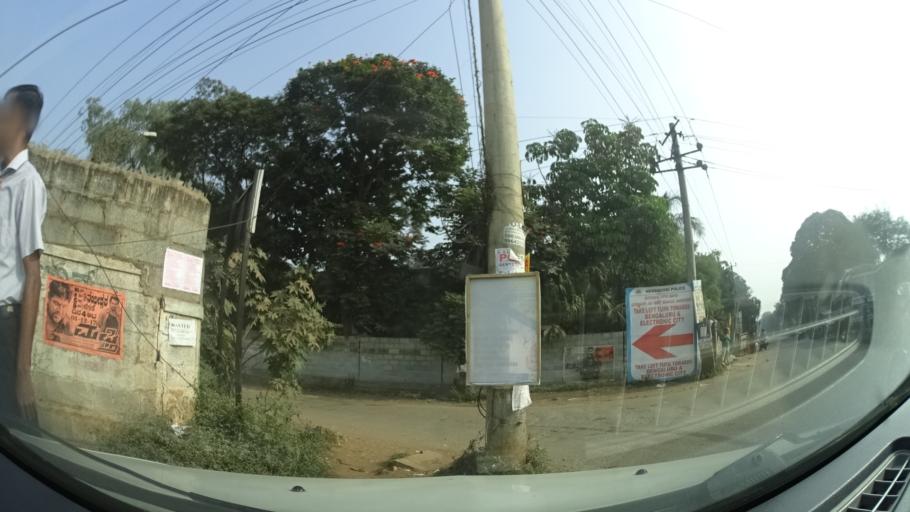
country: IN
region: Karnataka
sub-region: Bangalore Urban
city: Anekal
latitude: 12.8170
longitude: 77.6762
